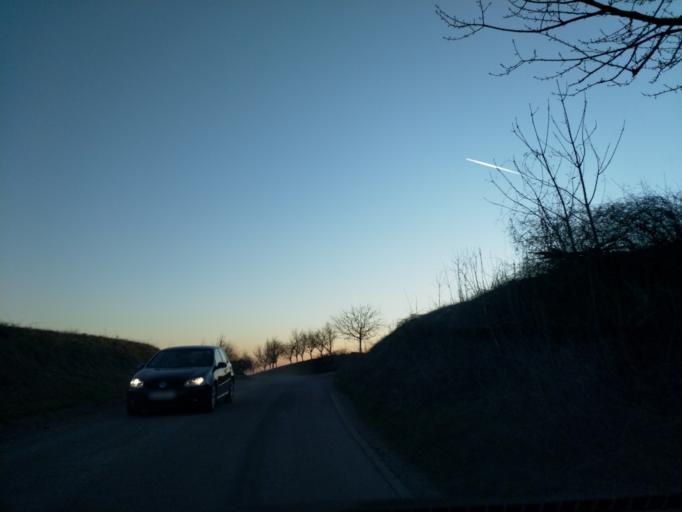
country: RS
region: Central Serbia
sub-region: Pomoravski Okrug
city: Paracin
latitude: 43.9271
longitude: 21.5124
